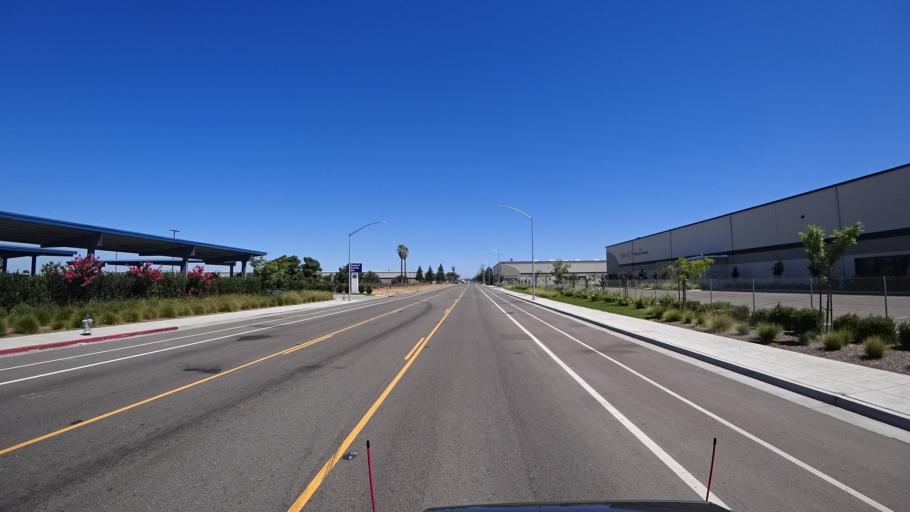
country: US
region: California
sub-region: Fresno County
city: Easton
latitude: 36.6846
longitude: -119.7727
